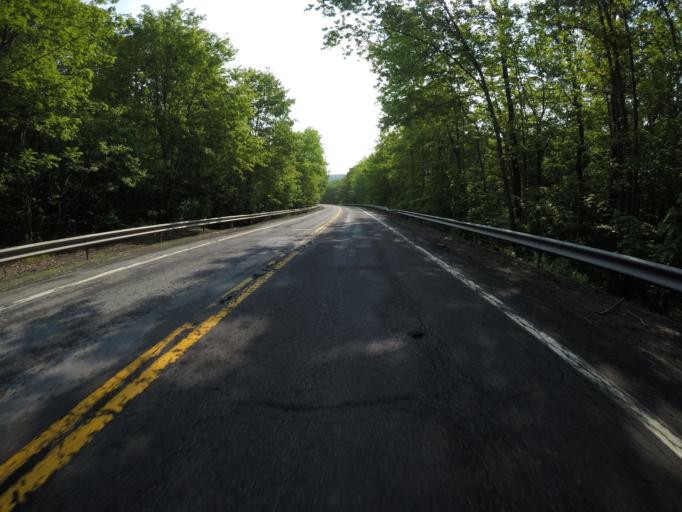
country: US
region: New York
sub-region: Sullivan County
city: Livingston Manor
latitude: 42.1036
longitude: -74.7873
